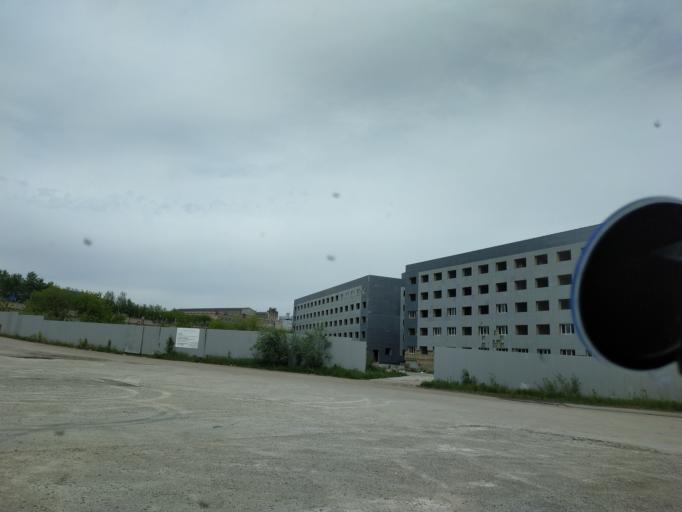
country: RU
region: Moskovskaya
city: Zhukovskiy
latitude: 55.5521
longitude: 38.1246
